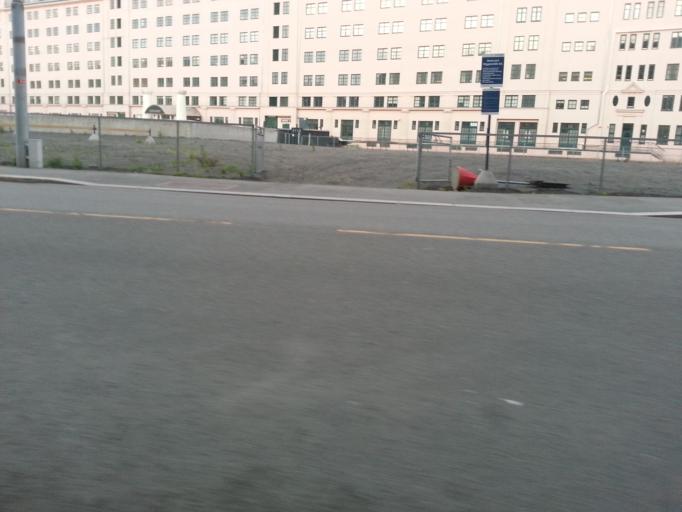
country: NO
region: Oslo
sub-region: Oslo
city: Oslo
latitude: 59.9077
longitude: 10.7448
